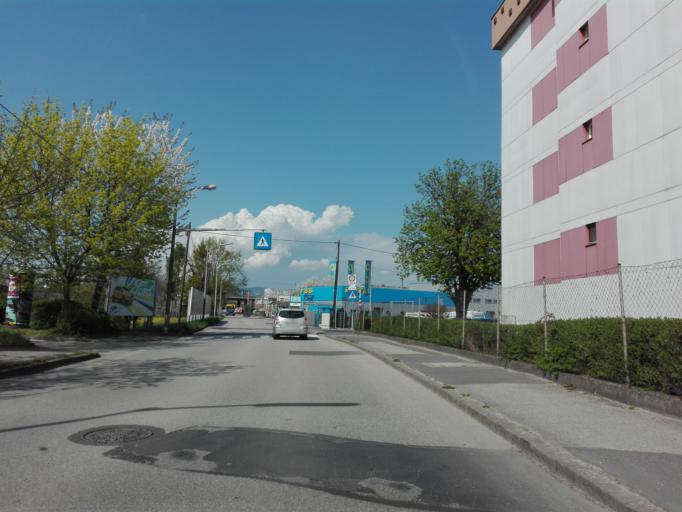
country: AT
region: Upper Austria
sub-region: Politischer Bezirk Linz-Land
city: Leonding
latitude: 48.2495
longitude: 14.2768
